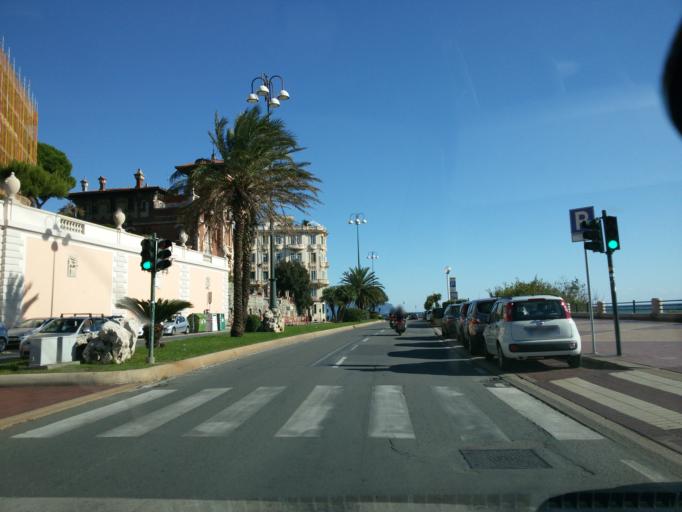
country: IT
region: Liguria
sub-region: Provincia di Genova
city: San Teodoro
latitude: 44.3924
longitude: 8.9541
